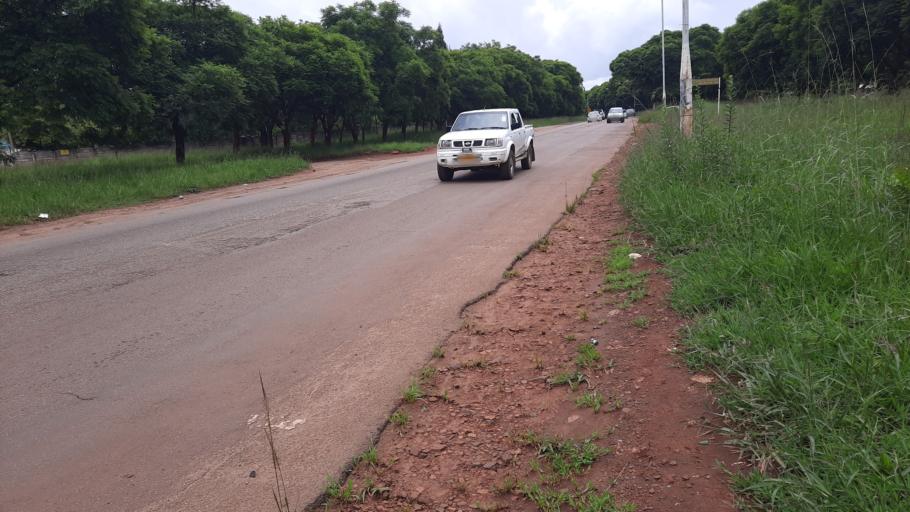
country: ZW
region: Harare
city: Harare
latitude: -17.8200
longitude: 31.0261
